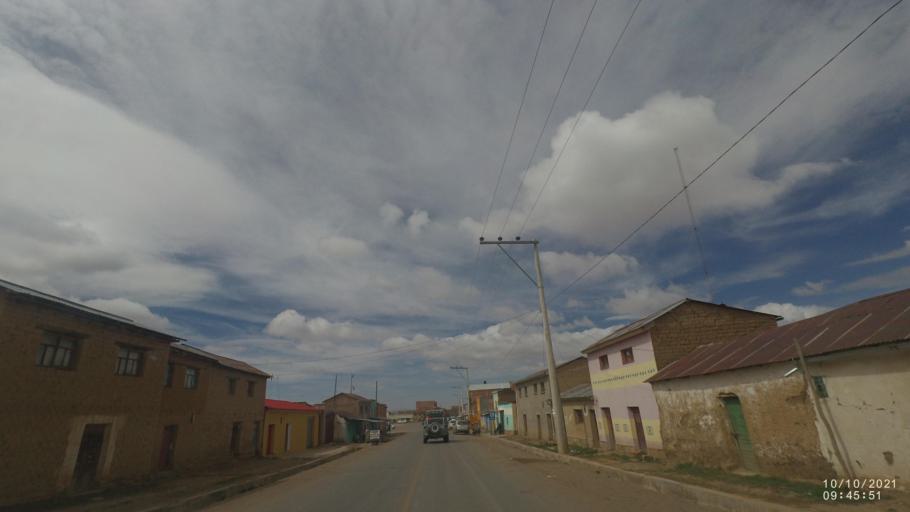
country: BO
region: La Paz
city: Quime
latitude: -17.1751
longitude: -67.3376
